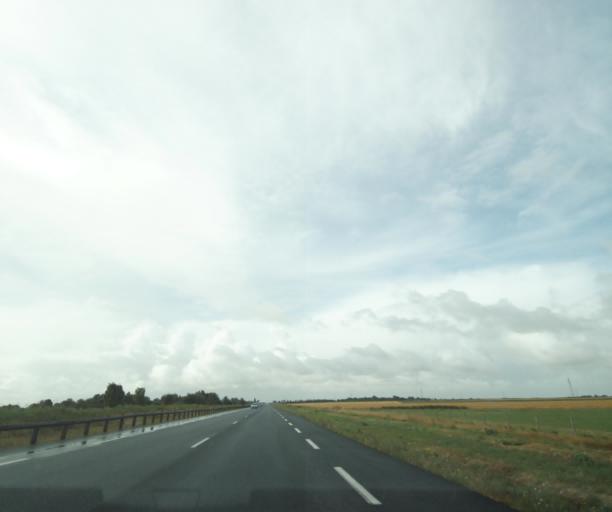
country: FR
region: Pays de la Loire
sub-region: Departement de la Vendee
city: Champagne-les-Marais
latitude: 46.3639
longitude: -1.0880
